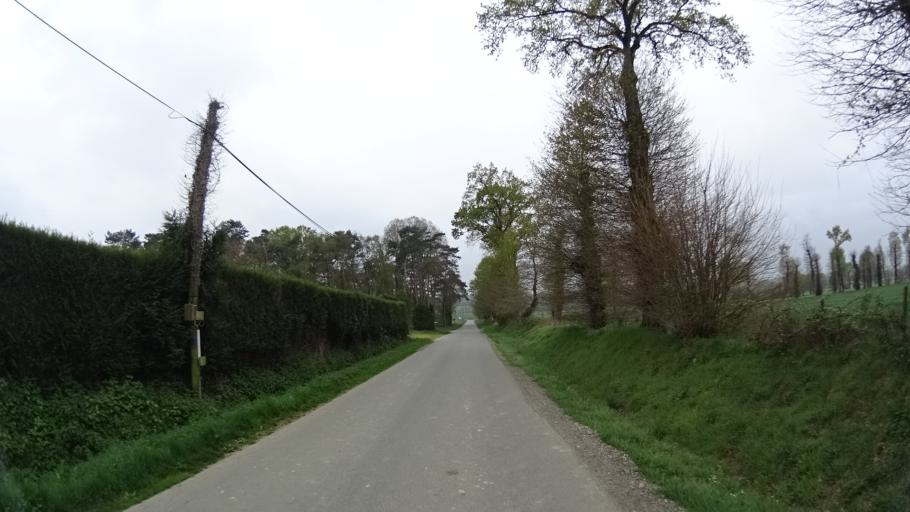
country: FR
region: Brittany
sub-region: Departement d'Ille-et-Vilaine
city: Saint-Gilles
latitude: 48.1412
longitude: -1.8455
